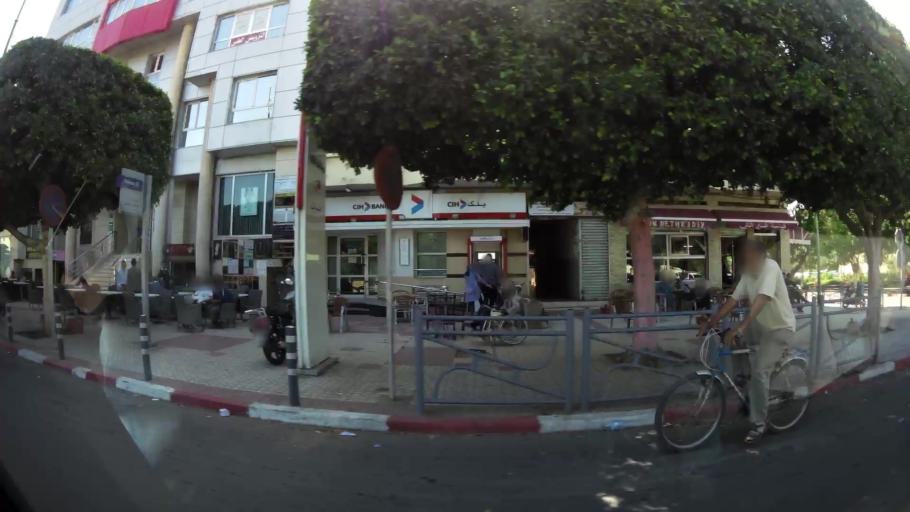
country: MA
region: Souss-Massa-Draa
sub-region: Inezgane-Ait Mellou
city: Inezgane
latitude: 30.3600
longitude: -9.5336
